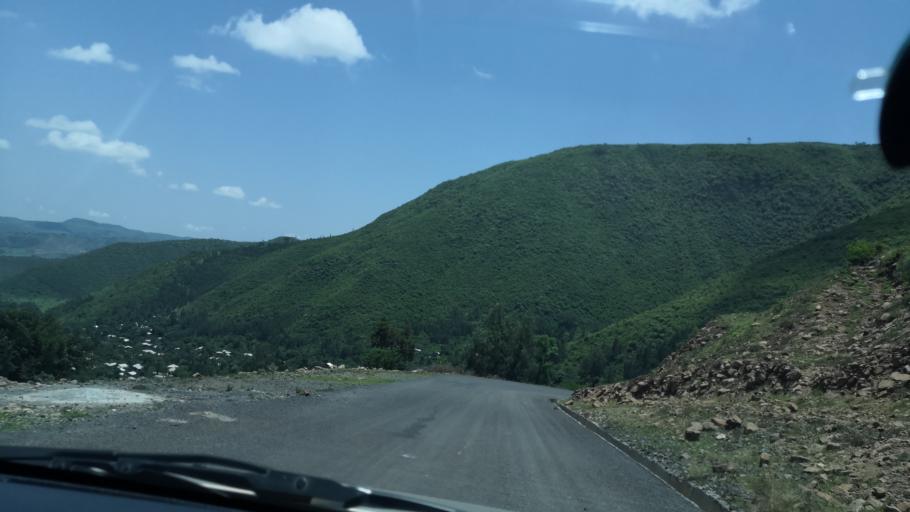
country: ET
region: Amhara
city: Abomsa
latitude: 10.3027
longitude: 39.8889
